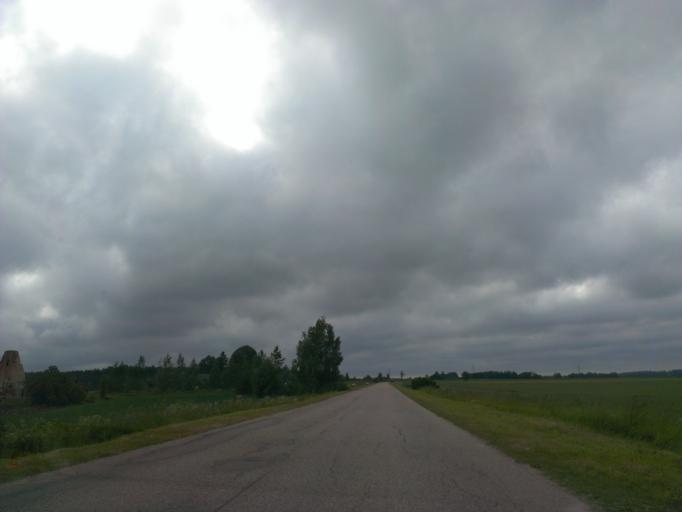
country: LV
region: Aizpute
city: Aizpute
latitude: 56.7162
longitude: 21.4594
